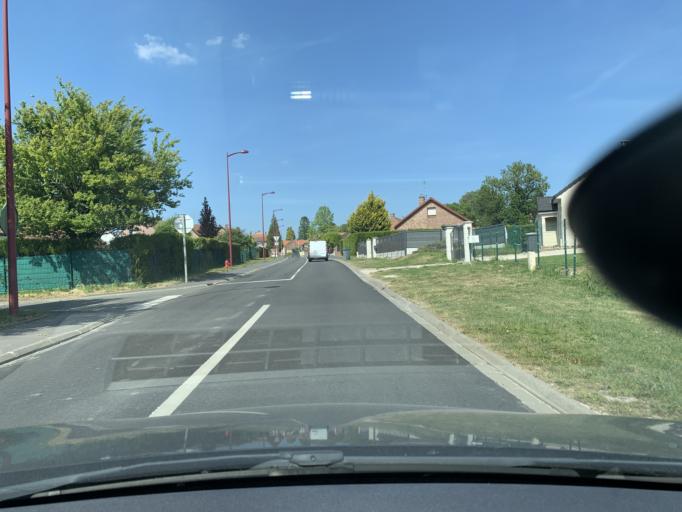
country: FR
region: Nord-Pas-de-Calais
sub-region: Departement du Pas-de-Calais
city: Oisy-le-Verger
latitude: 50.2446
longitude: 3.1173
